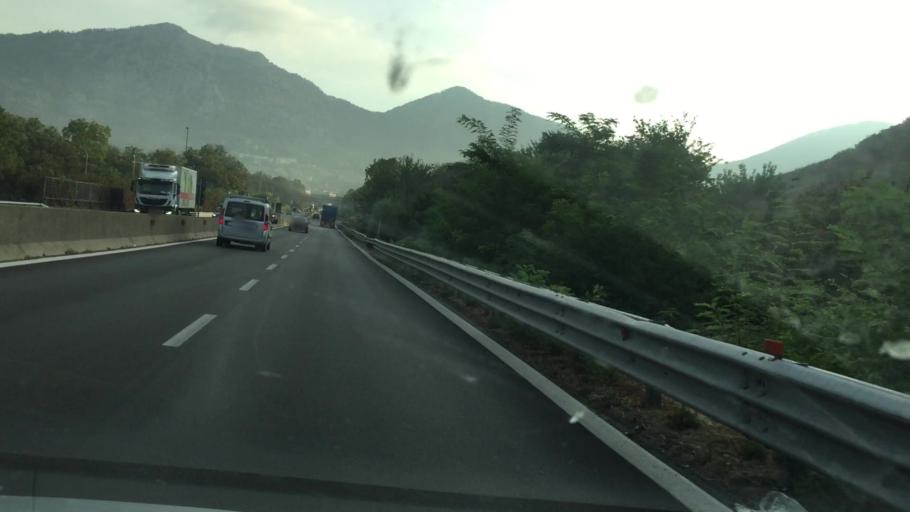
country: IT
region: Campania
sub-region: Provincia di Avellino
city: Torchiati
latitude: 40.8273
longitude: 14.8139
